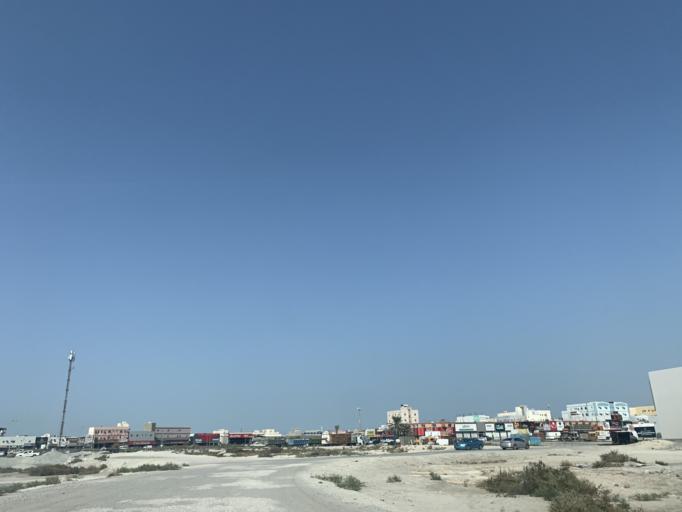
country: BH
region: Central Governorate
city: Madinat Hamad
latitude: 26.1370
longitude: 50.4899
